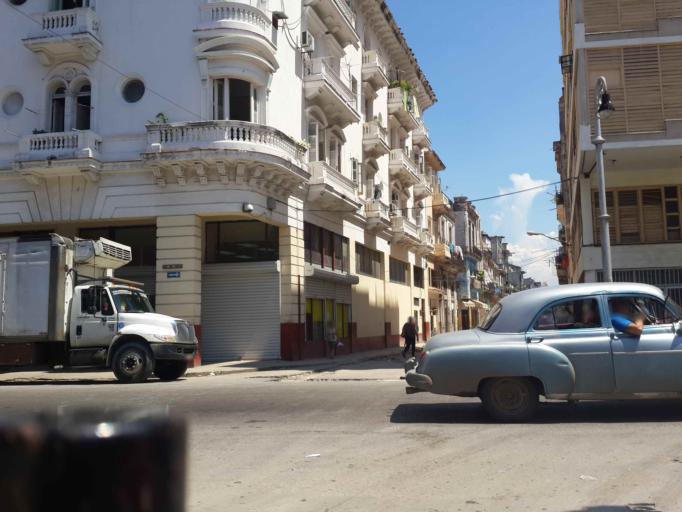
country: CU
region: La Habana
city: Centro Habana
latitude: 23.1402
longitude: -82.3637
